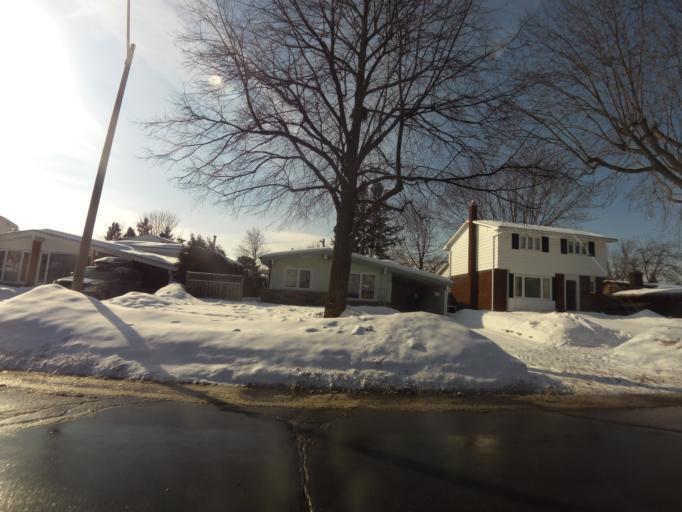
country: CA
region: Ontario
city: Ottawa
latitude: 45.3860
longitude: -75.6365
